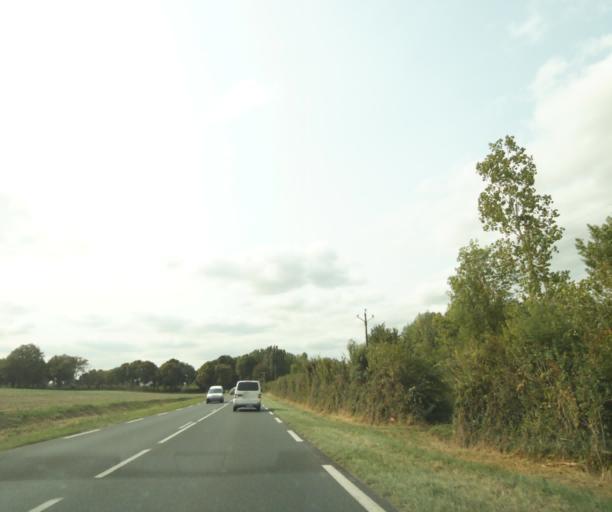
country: FR
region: Centre
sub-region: Departement de l'Indre
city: Chatillon-sur-Indre
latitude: 46.9684
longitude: 1.1989
